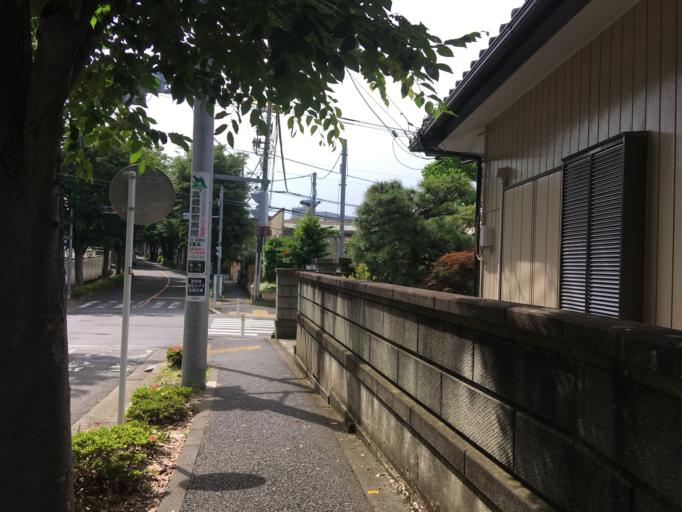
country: JP
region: Kanagawa
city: Minami-rinkan
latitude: 35.5088
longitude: 139.4696
